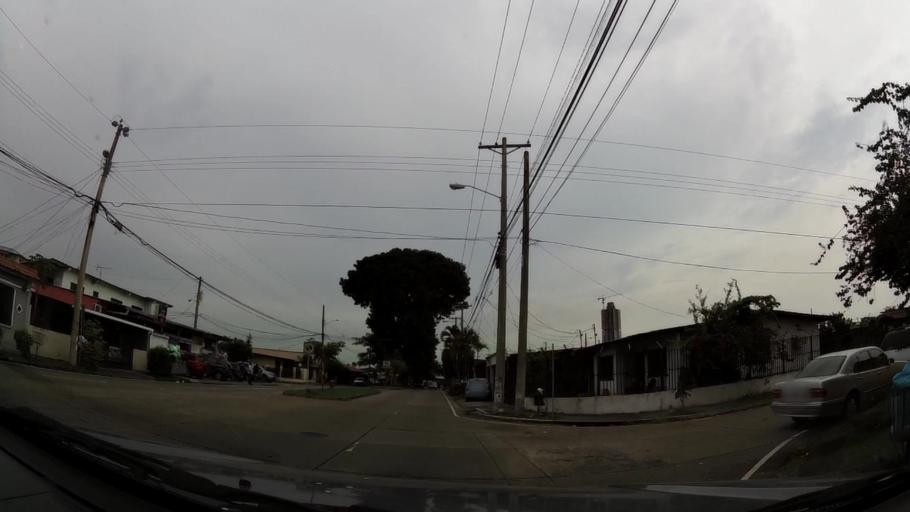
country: PA
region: Panama
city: San Miguelito
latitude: 9.0261
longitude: -79.4726
